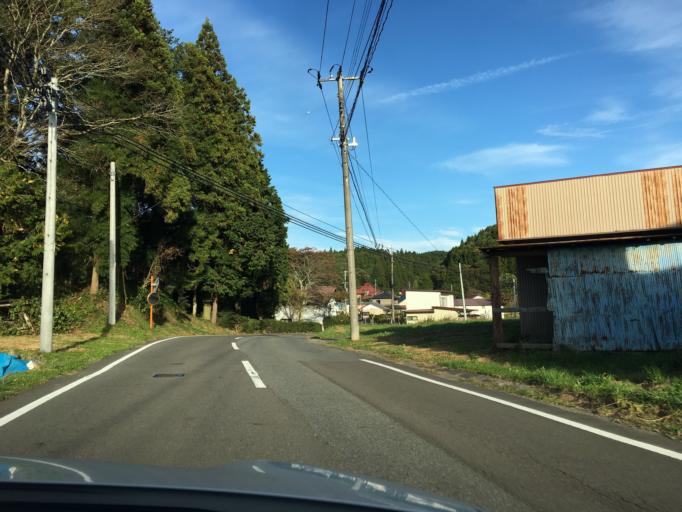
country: JP
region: Fukushima
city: Ishikawa
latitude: 37.1904
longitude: 140.5807
